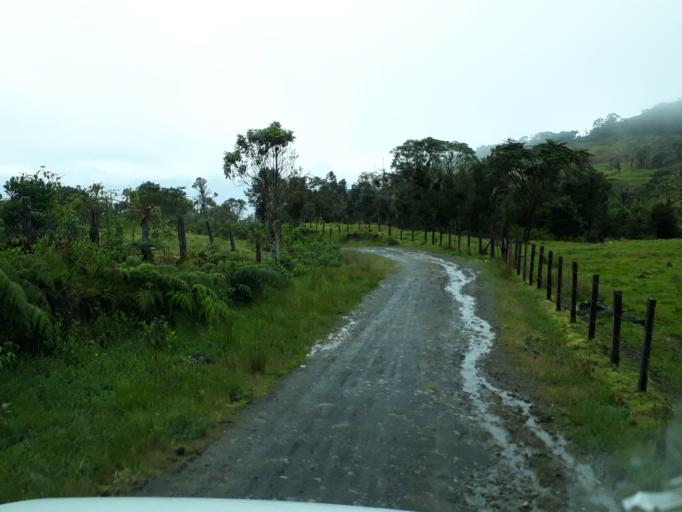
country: CO
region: Cundinamarca
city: Junin
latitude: 4.7187
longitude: -73.6281
